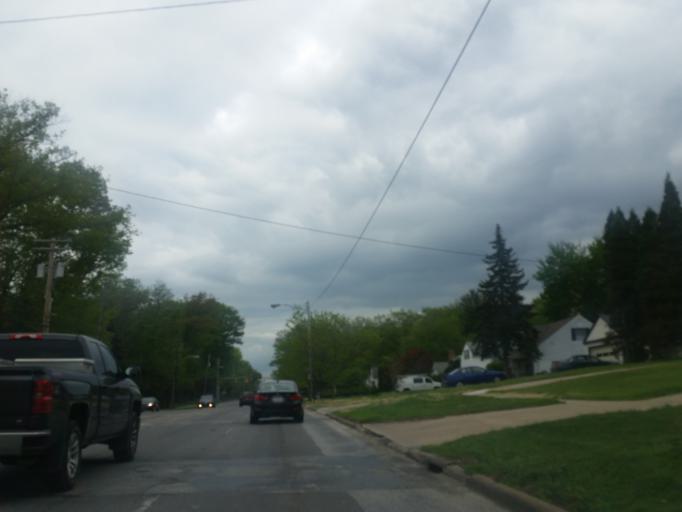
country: US
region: Ohio
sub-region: Cuyahoga County
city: South Euclid
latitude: 41.5013
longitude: -81.5106
